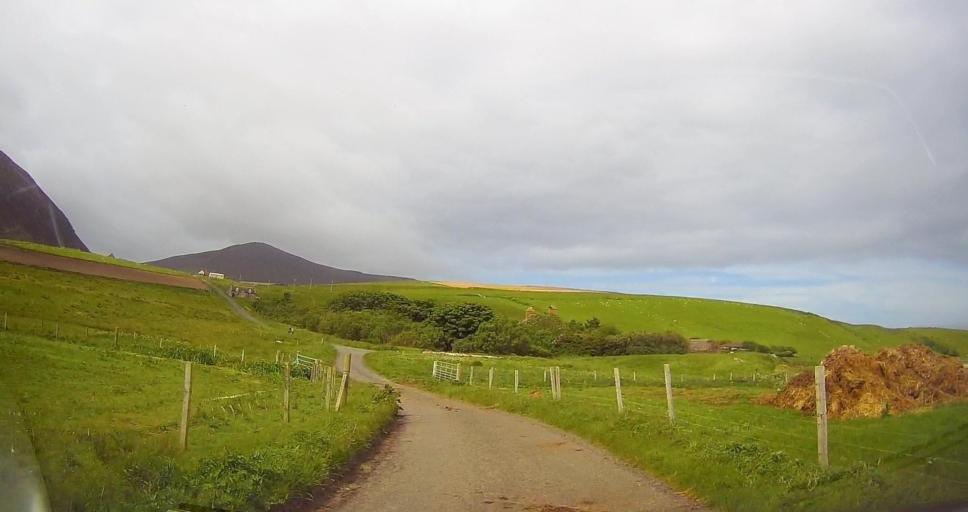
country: GB
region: Scotland
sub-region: Orkney Islands
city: Stromness
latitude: 58.9164
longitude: -3.3218
